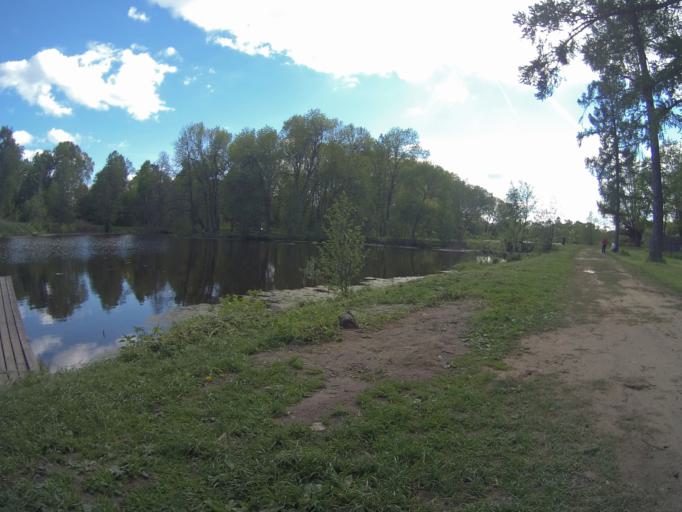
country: RU
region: Vladimir
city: Muromtsevo
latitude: 55.9269
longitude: 40.9051
